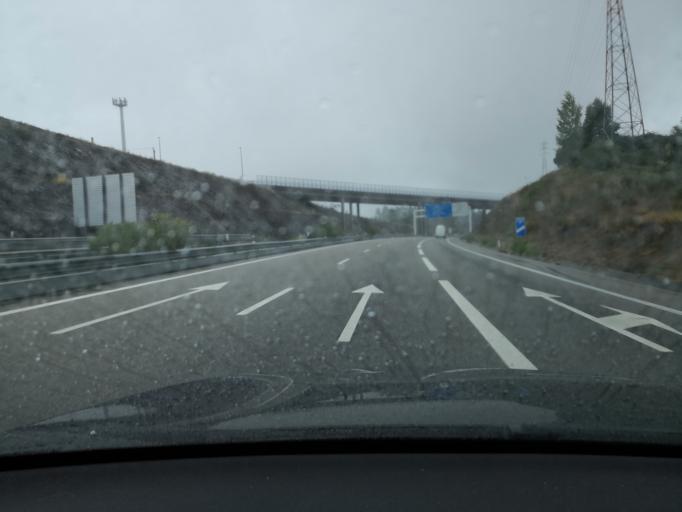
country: PT
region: Porto
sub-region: Pacos de Ferreira
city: Seroa
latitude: 41.2452
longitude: -8.4354
